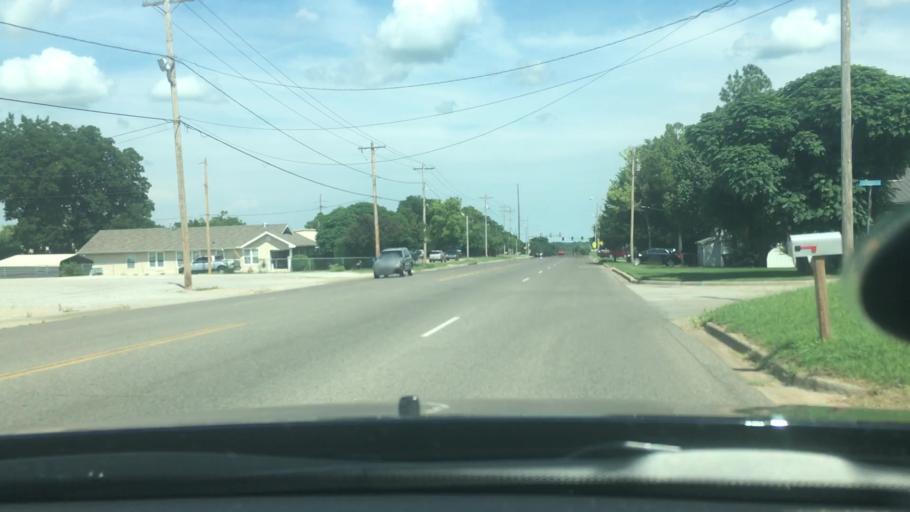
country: US
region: Oklahoma
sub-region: Pottawatomie County
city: Shawnee
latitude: 35.3326
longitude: -96.8978
